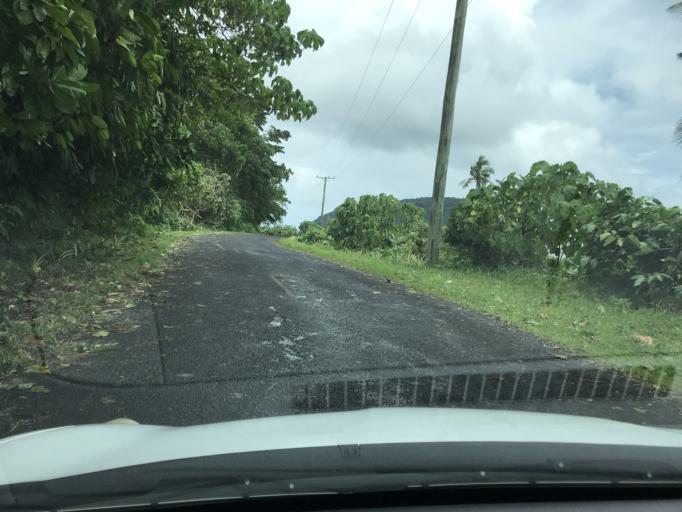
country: WS
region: Va`a-o-Fonoti
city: Samamea
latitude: -14.0463
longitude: -171.4438
